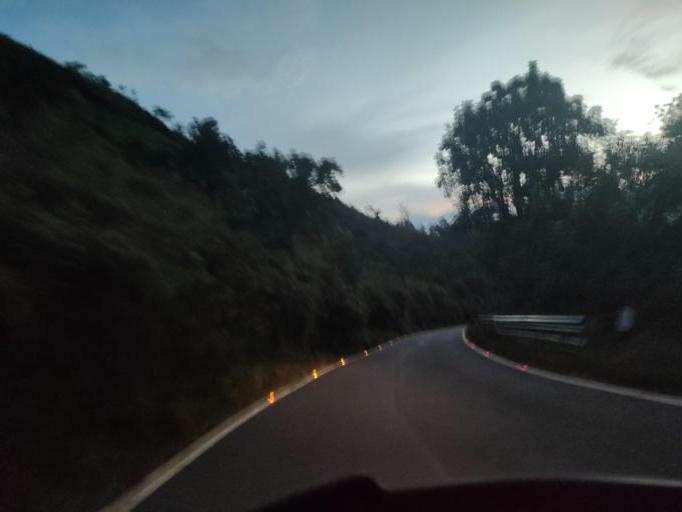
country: IN
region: Tamil Nadu
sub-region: Dindigul
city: Kodaikanal
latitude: 10.2828
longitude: 77.5382
